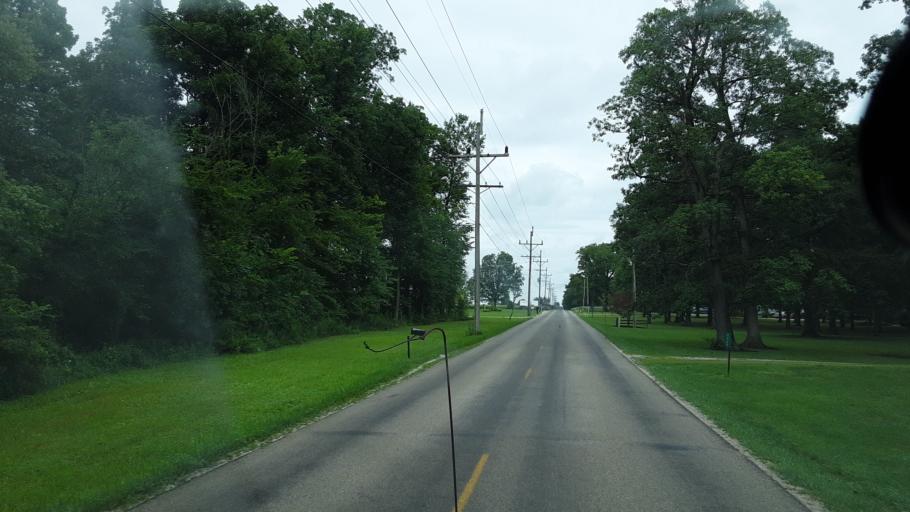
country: US
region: Indiana
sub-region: Jay County
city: Portland
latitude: 40.4597
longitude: -85.0202
